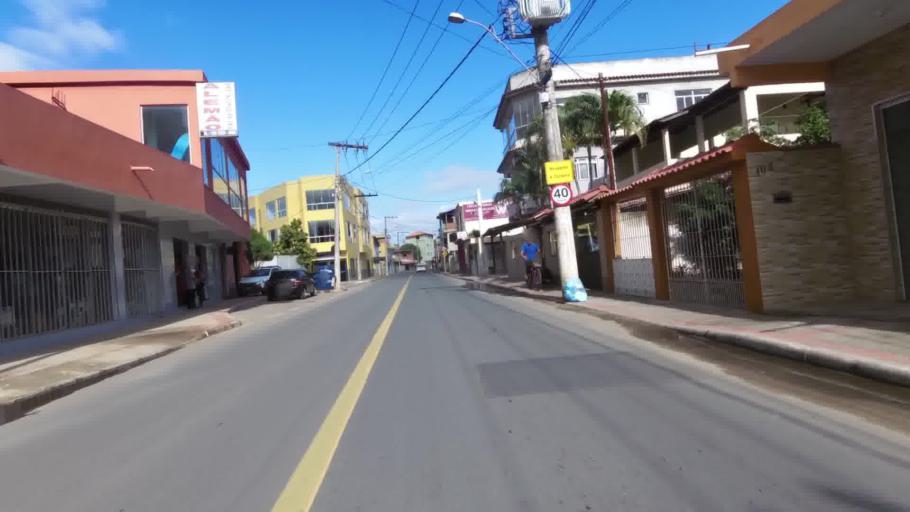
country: BR
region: Espirito Santo
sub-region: Piuma
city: Piuma
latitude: -20.8394
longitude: -40.7310
